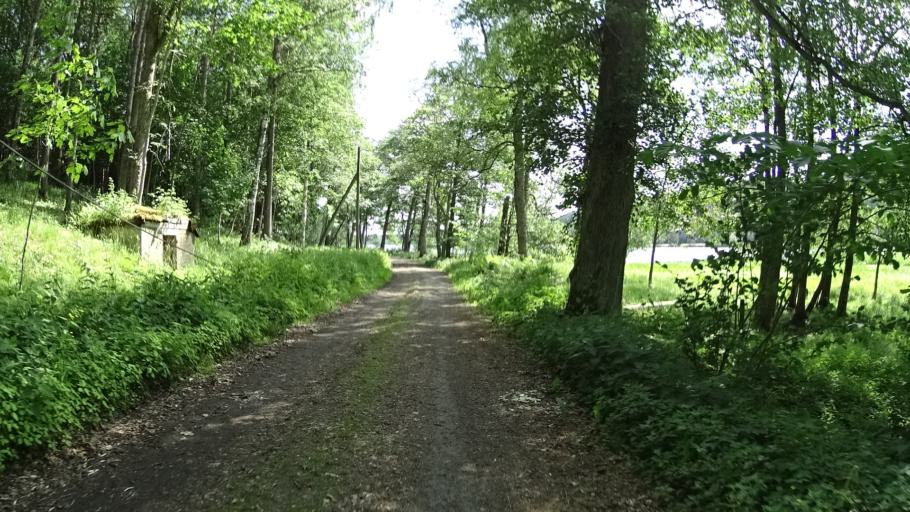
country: FI
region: Uusimaa
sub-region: Raaseporin
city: Pohja
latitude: 60.1209
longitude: 23.5390
